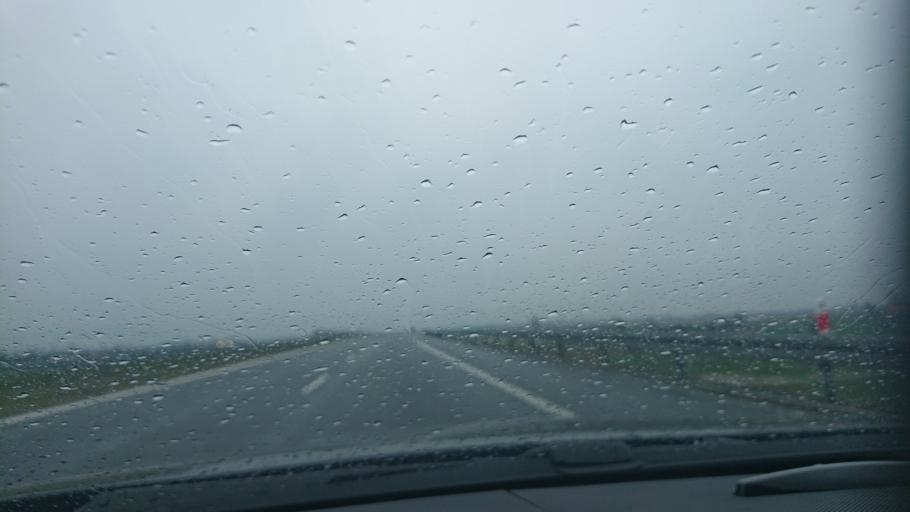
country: PL
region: Greater Poland Voivodeship
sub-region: Powiat gnieznienski
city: Gniezno
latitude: 52.5622
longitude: 17.5525
